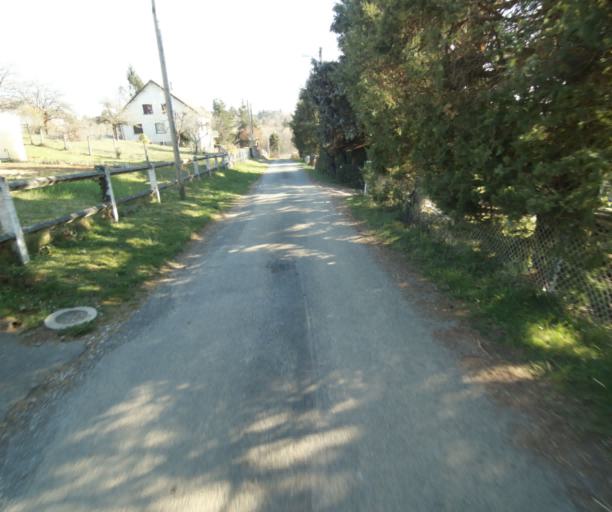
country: FR
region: Limousin
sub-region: Departement de la Correze
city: Saint-Clement
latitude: 45.3401
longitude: 1.6737
